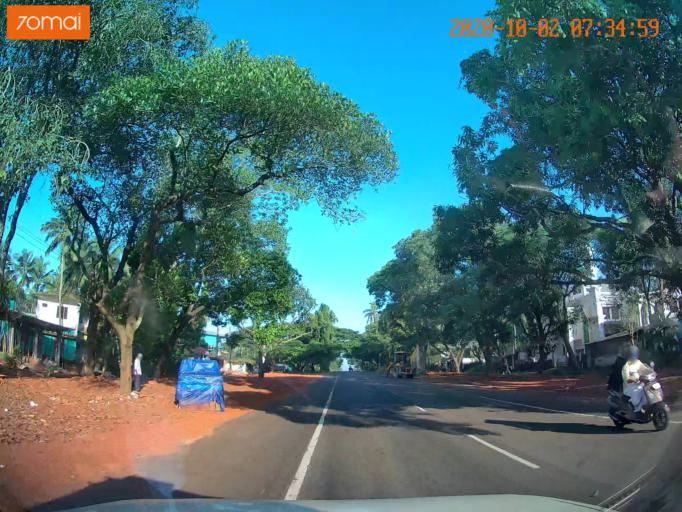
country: IN
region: Kerala
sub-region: Malappuram
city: Pariyapuram
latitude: 11.0666
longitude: 75.9243
